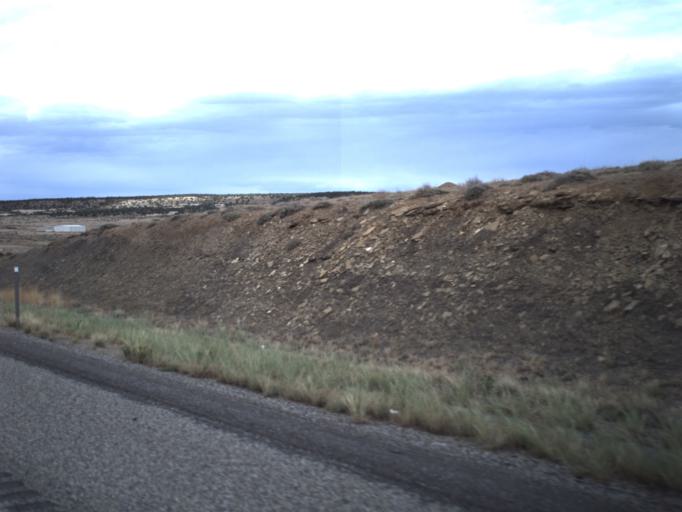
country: US
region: Colorado
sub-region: Mesa County
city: Loma
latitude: 39.1444
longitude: -109.1520
